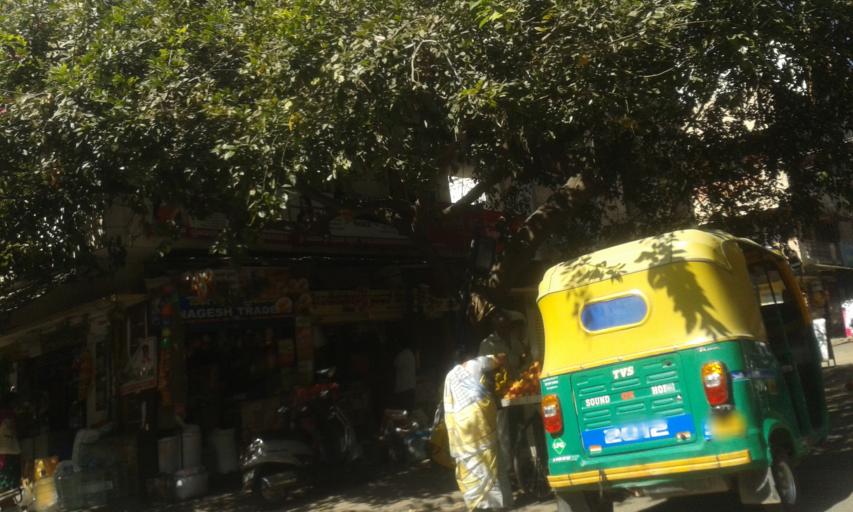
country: IN
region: Karnataka
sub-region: Bangalore Urban
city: Bangalore
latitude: 12.9190
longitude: 77.5915
